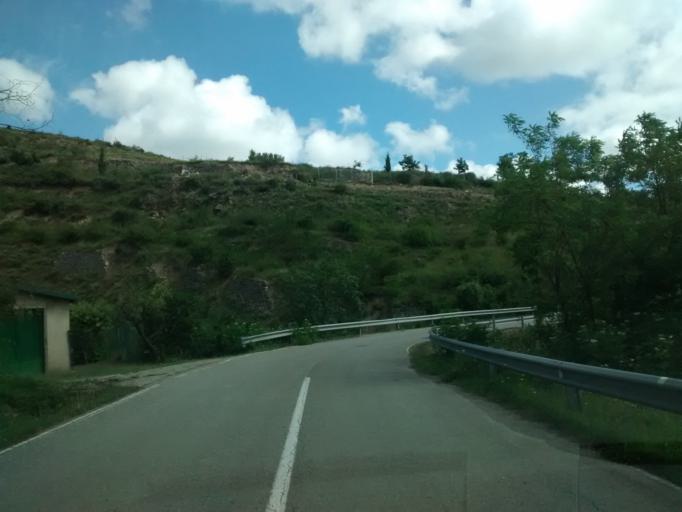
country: ES
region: La Rioja
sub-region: Provincia de La Rioja
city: Soto en Cameros
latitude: 42.2830
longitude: -2.4314
